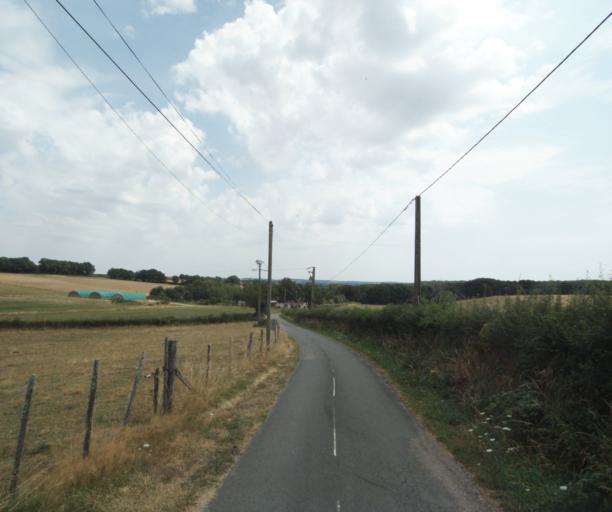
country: FR
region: Bourgogne
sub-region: Departement de Saone-et-Loire
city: Gueugnon
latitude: 46.5913
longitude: 4.0129
